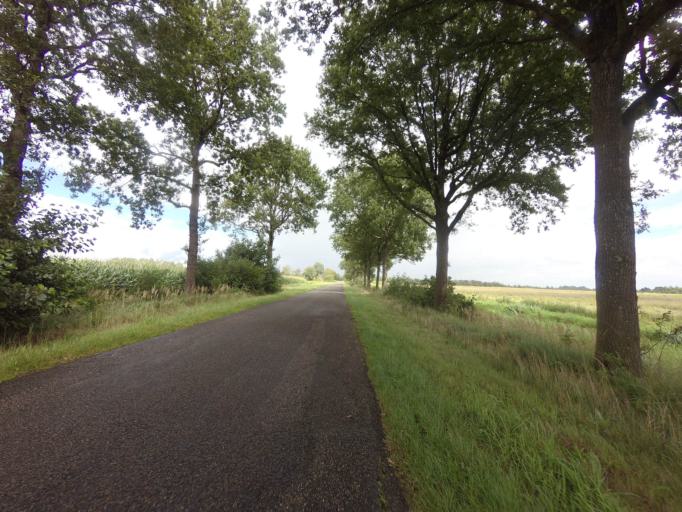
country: NL
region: Drenthe
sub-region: Gemeente Westerveld
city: Dwingeloo
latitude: 52.9852
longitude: 6.3714
